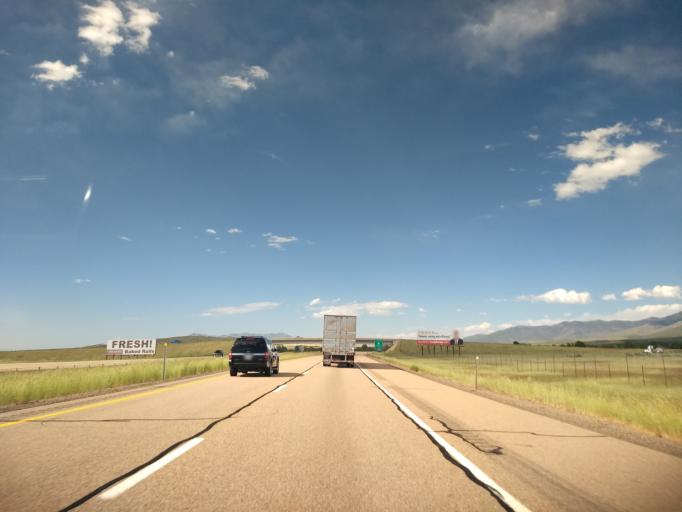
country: US
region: Utah
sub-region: Millard County
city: Fillmore
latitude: 38.9760
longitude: -112.3397
